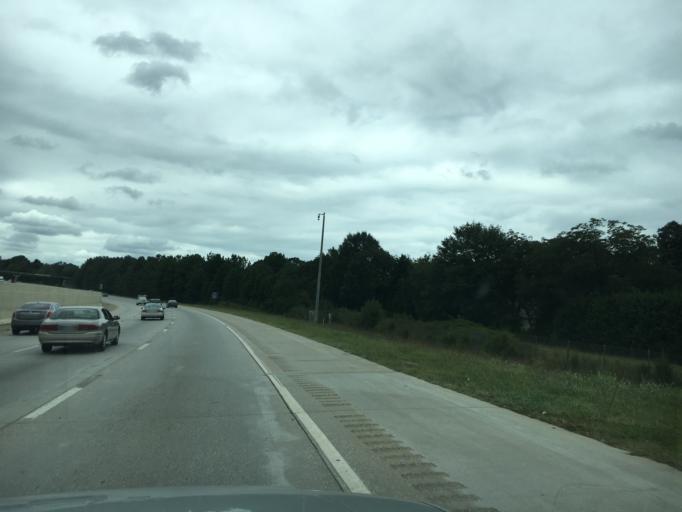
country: US
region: South Carolina
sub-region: Greenville County
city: Mauldin
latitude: 34.7733
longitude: -82.2725
